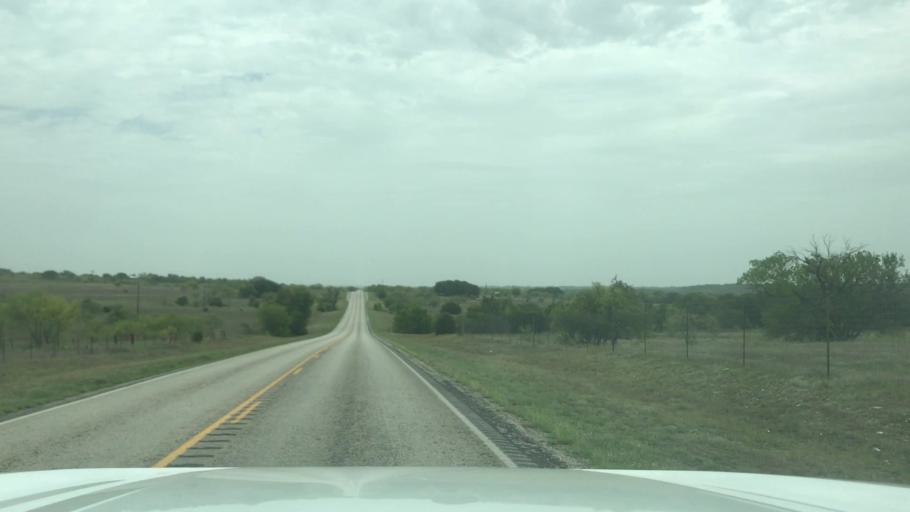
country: US
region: Texas
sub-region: Hamilton County
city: Hico
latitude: 32.0528
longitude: -98.1705
